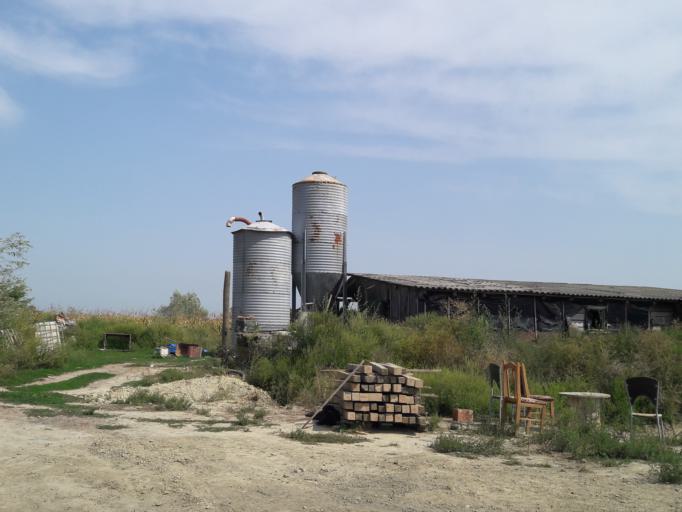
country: HR
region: Osjecko-Baranjska
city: Brijest
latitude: 45.5167
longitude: 18.6309
